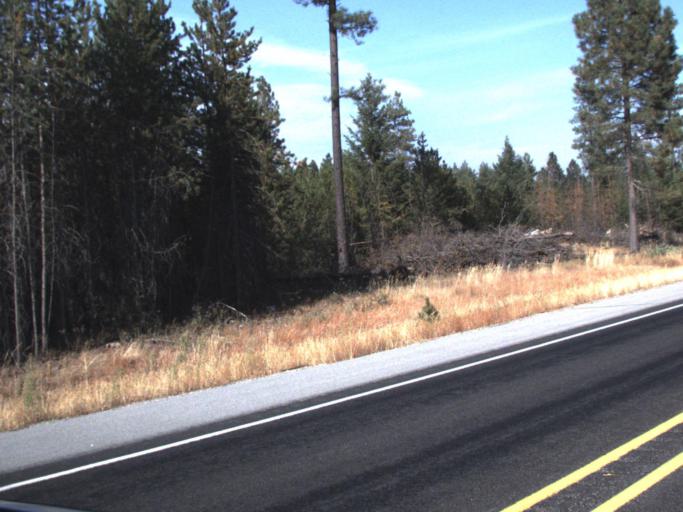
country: US
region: Washington
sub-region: Pend Oreille County
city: Newport
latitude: 48.1441
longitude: -117.1463
